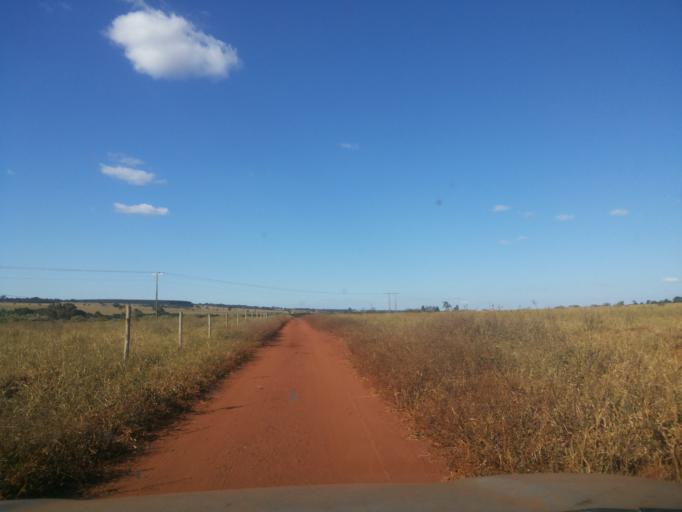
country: BR
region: Minas Gerais
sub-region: Centralina
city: Centralina
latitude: -18.7364
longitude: -49.1783
